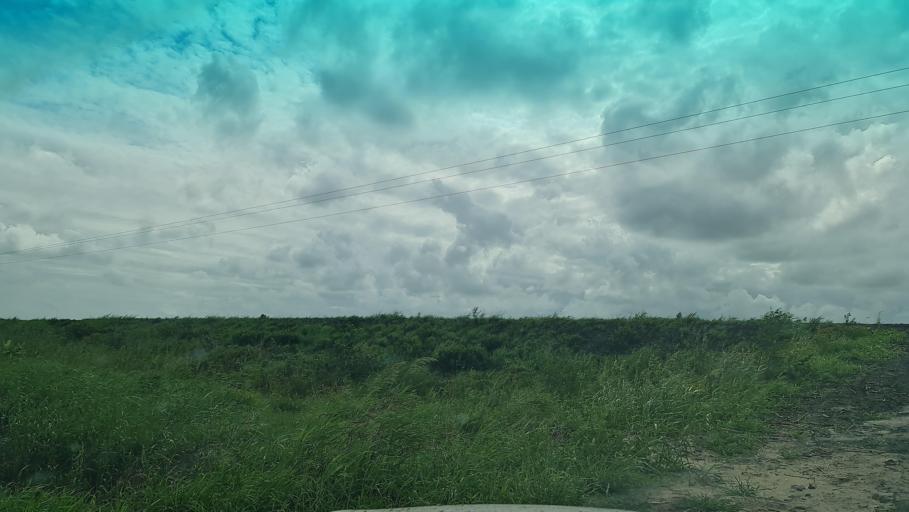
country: MZ
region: Maputo
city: Manhica
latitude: -25.4653
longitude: 32.8179
